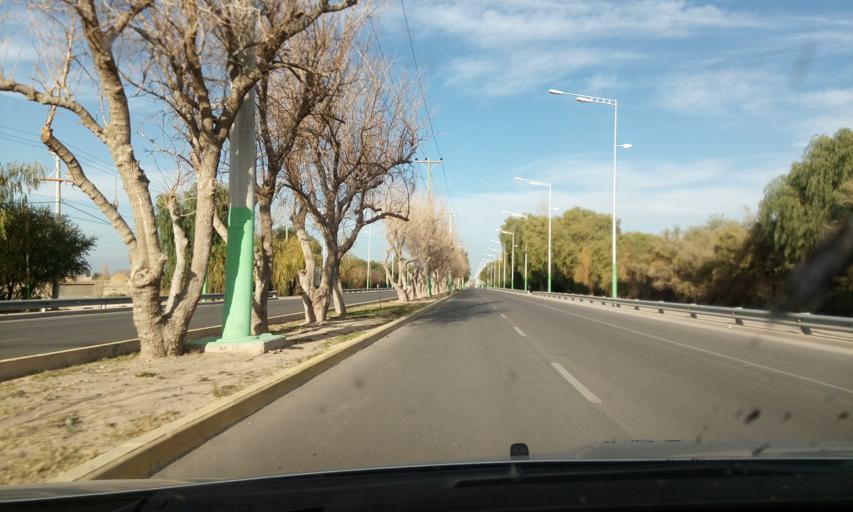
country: AR
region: San Juan
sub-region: Departamento de Rivadavia
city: Rivadavia
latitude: -31.5262
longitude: -68.6102
